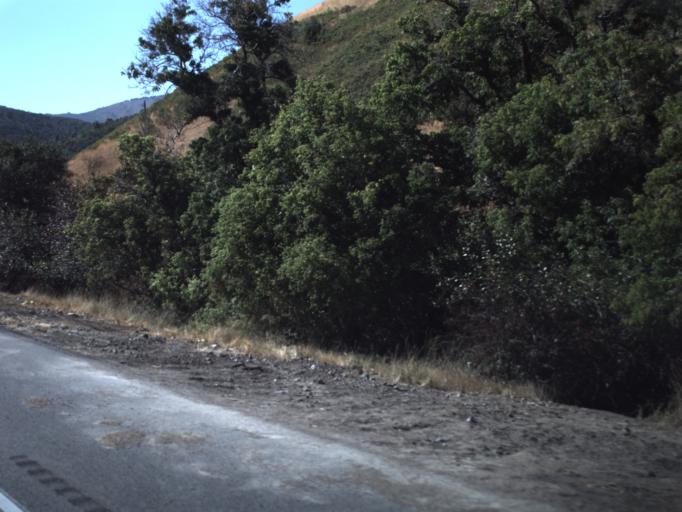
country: US
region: Utah
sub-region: Cache County
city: Wellsville
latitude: 41.6016
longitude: -111.9481
